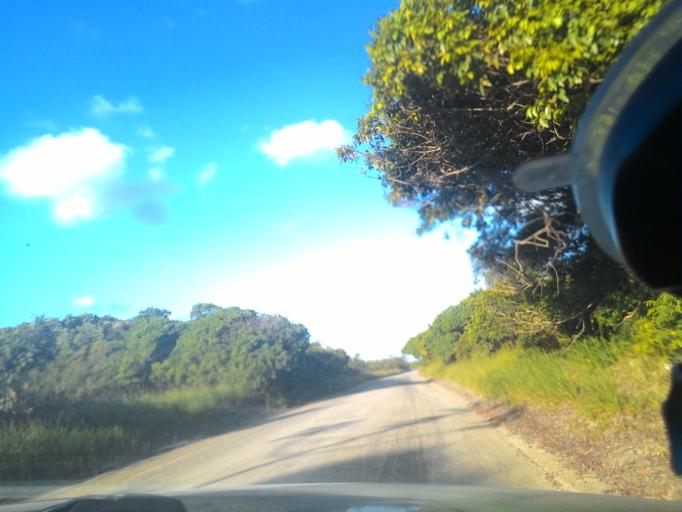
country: BR
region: Sao Paulo
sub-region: Pariquera-Acu
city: Pariquera Acu
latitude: -24.8863
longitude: -47.7437
